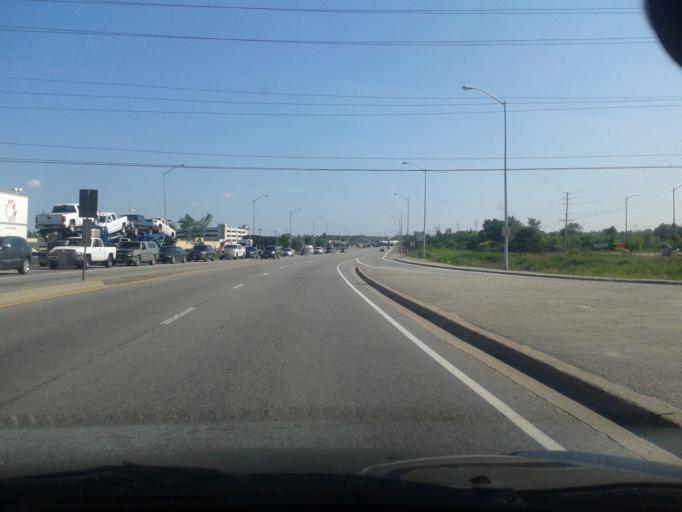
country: CA
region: Ontario
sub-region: Nipissing District
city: North Bay
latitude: 46.3181
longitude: -79.4436
